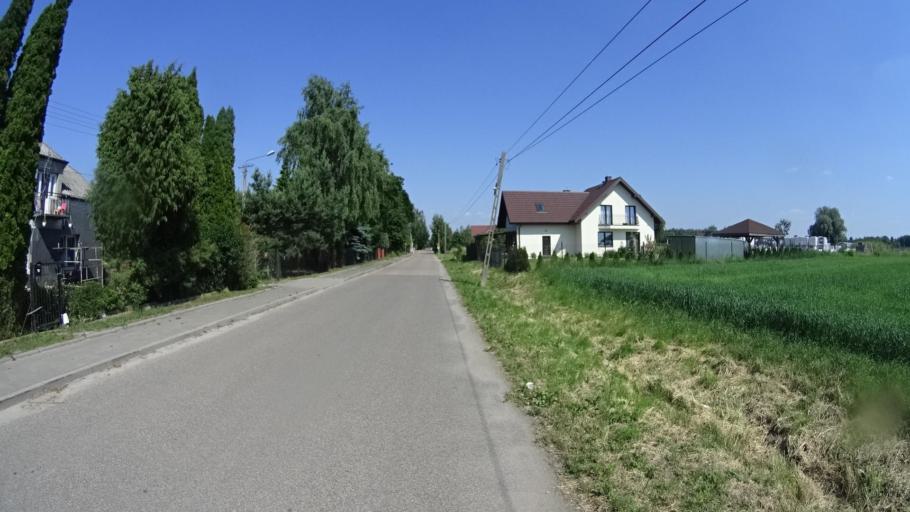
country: PL
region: Masovian Voivodeship
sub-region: Powiat warszawski zachodni
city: Bieniewice
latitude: 52.1909
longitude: 20.5454
